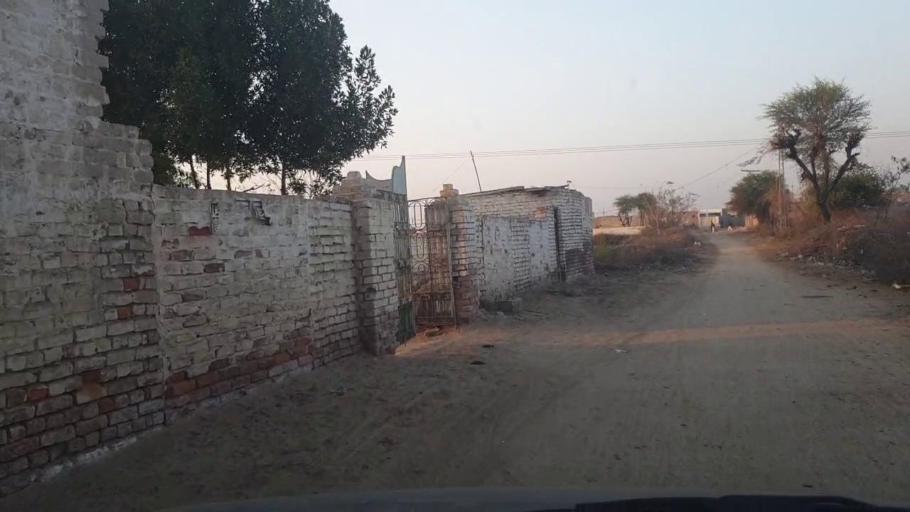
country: PK
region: Sindh
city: Bhit Shah
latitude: 25.8743
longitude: 68.5432
